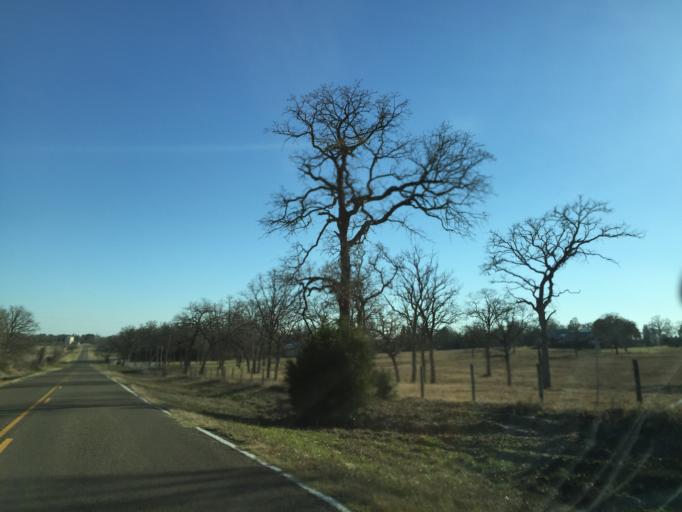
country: US
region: Texas
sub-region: Bastrop County
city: Elgin
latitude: 30.3936
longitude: -97.2467
